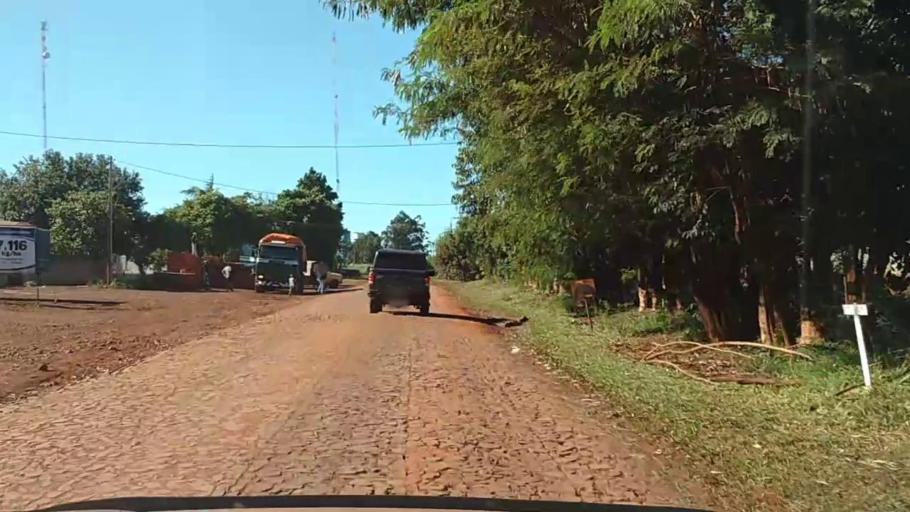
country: PY
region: Alto Parana
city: Naranjal
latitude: -25.8950
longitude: -55.4619
